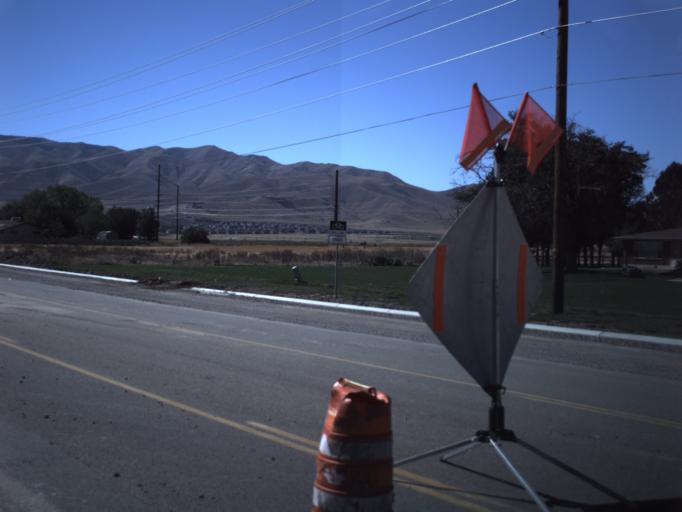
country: US
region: Utah
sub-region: Utah County
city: Saratoga Springs
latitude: 40.3573
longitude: -111.9162
